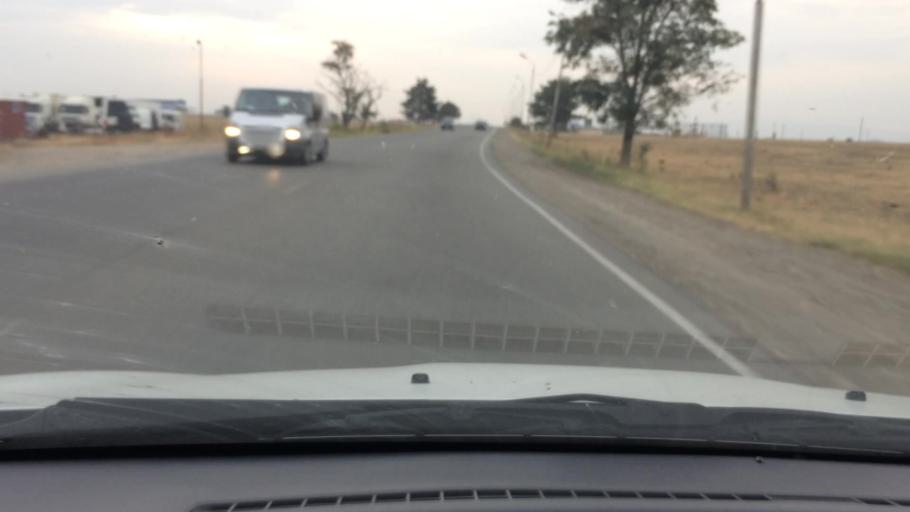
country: GE
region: Kvemo Kartli
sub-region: Marneuli
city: Marneuli
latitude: 41.5133
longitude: 44.7889
